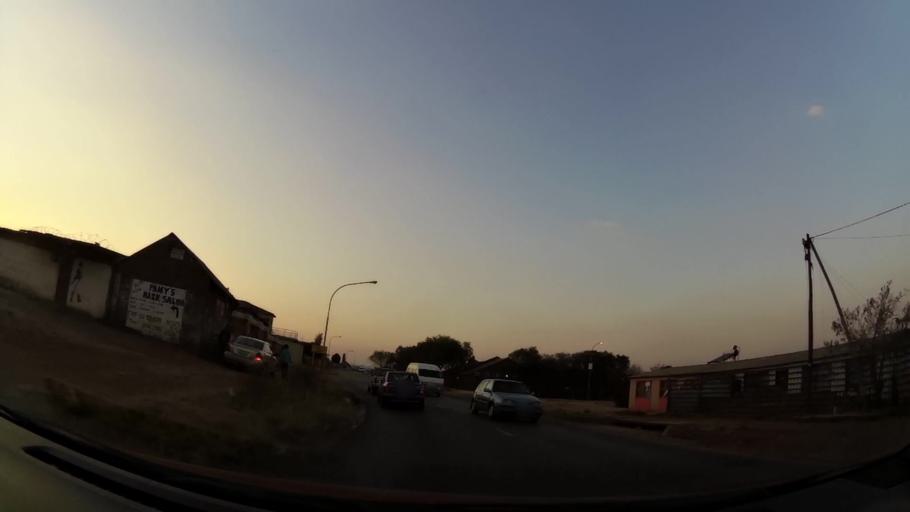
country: ZA
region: Gauteng
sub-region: City of Johannesburg Metropolitan Municipality
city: Soweto
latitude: -26.2899
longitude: 27.8808
